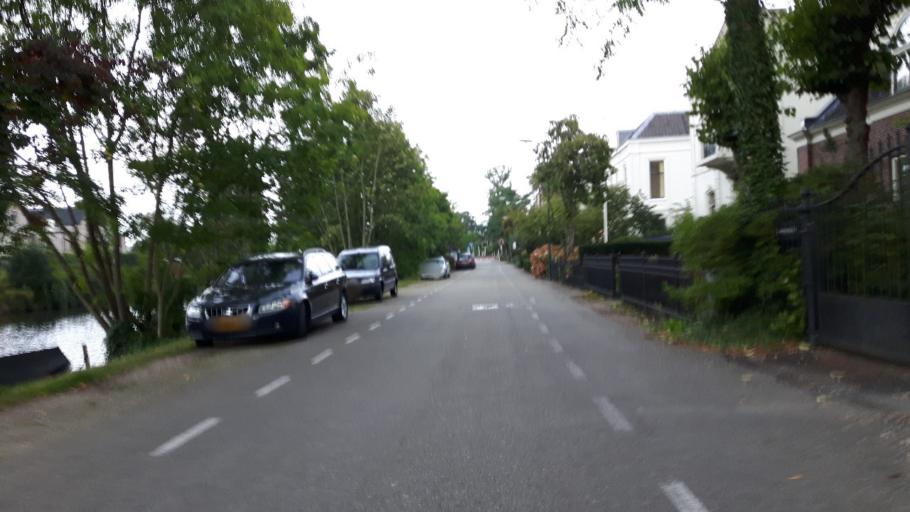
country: NL
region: Utrecht
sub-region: Stichtse Vecht
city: Maarssen
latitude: 52.1389
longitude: 5.0449
